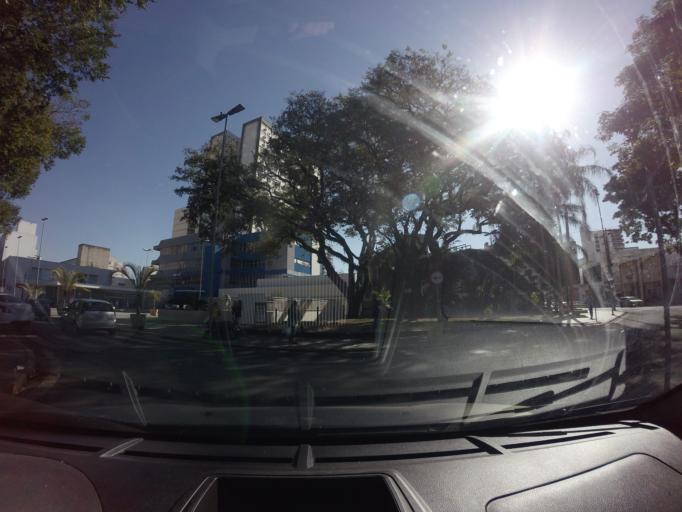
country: BR
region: Sao Paulo
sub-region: Piracicaba
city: Piracicaba
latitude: -22.7236
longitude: -47.6487
